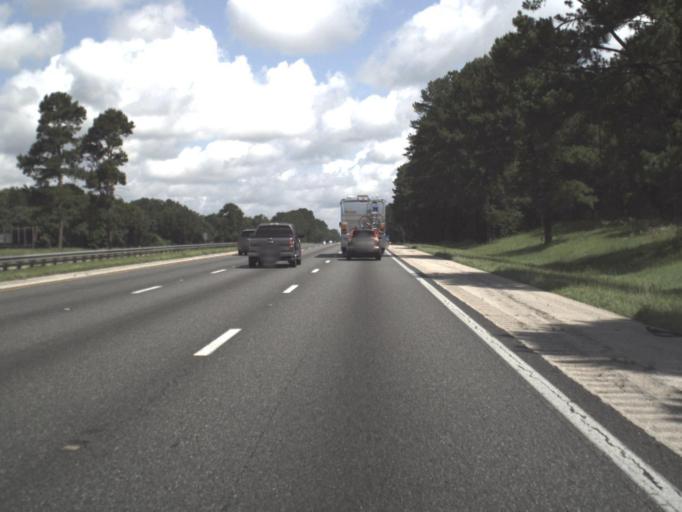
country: US
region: Florida
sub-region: Alachua County
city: High Springs
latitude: 29.8270
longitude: -82.5211
